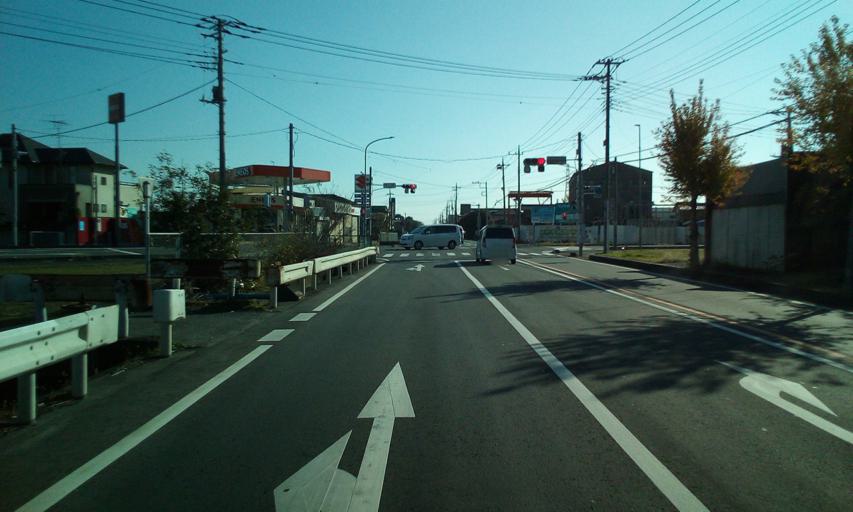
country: JP
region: Saitama
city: Kasukabe
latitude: 36.0106
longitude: 139.7933
